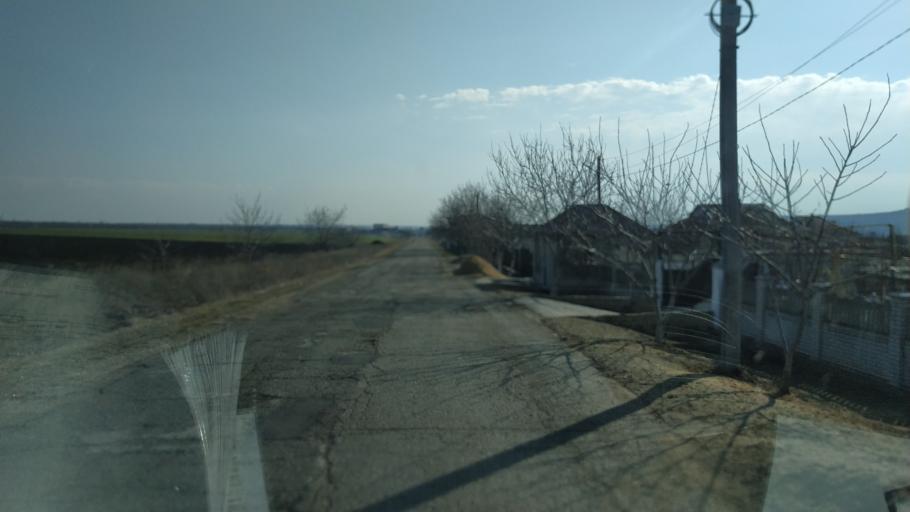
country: MD
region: Chisinau
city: Singera
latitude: 46.6885
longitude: 29.0442
